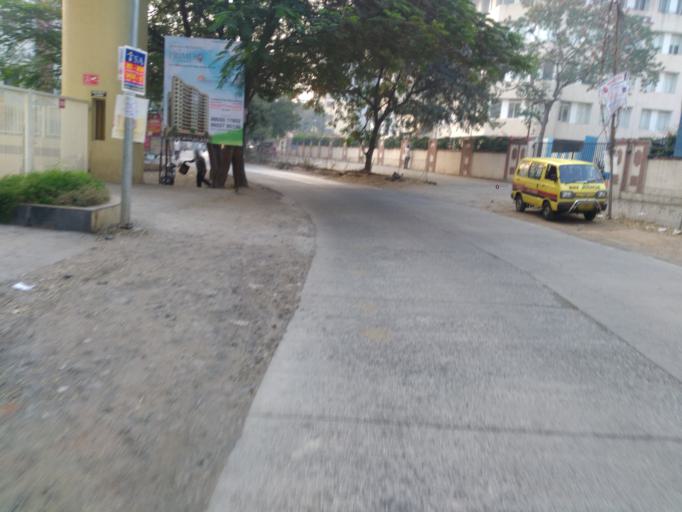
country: IN
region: Maharashtra
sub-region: Pune Division
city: Pune
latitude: 18.4546
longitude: 73.9139
